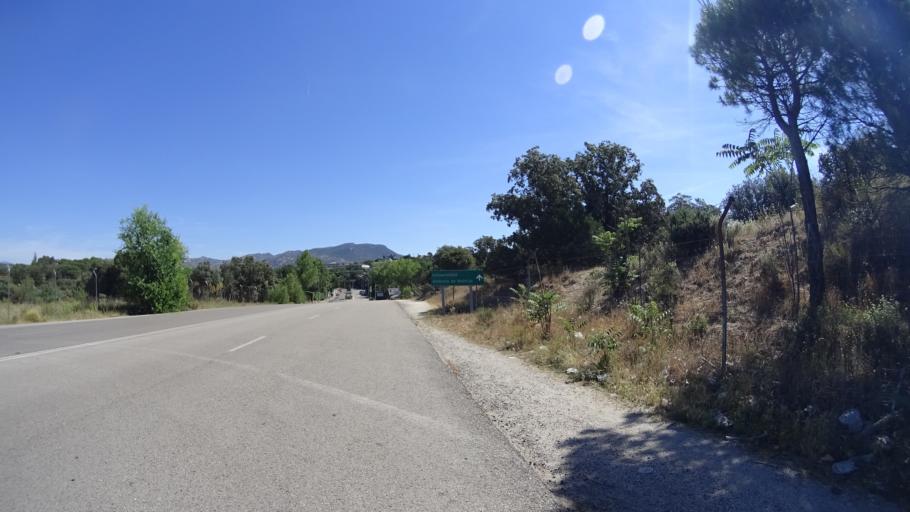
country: ES
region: Madrid
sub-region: Provincia de Madrid
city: Torrelodones
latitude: 40.5969
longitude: -3.9494
